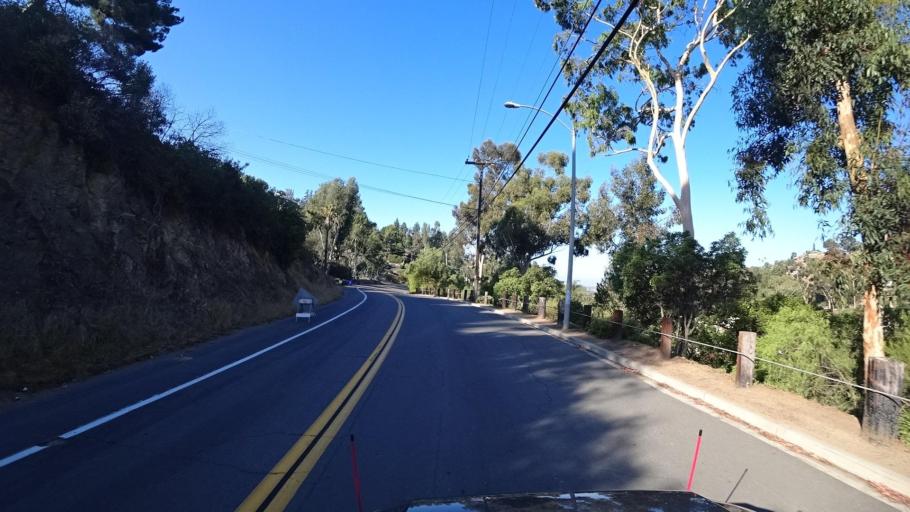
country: US
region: California
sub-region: San Diego County
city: Casa de Oro-Mount Helix
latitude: 32.7717
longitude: -116.9833
